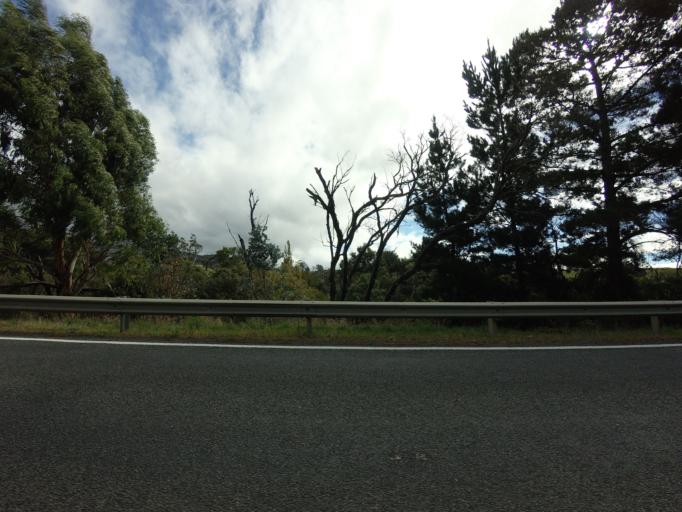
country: AU
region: Tasmania
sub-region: Derwent Valley
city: New Norfolk
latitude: -42.7346
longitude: 146.9535
